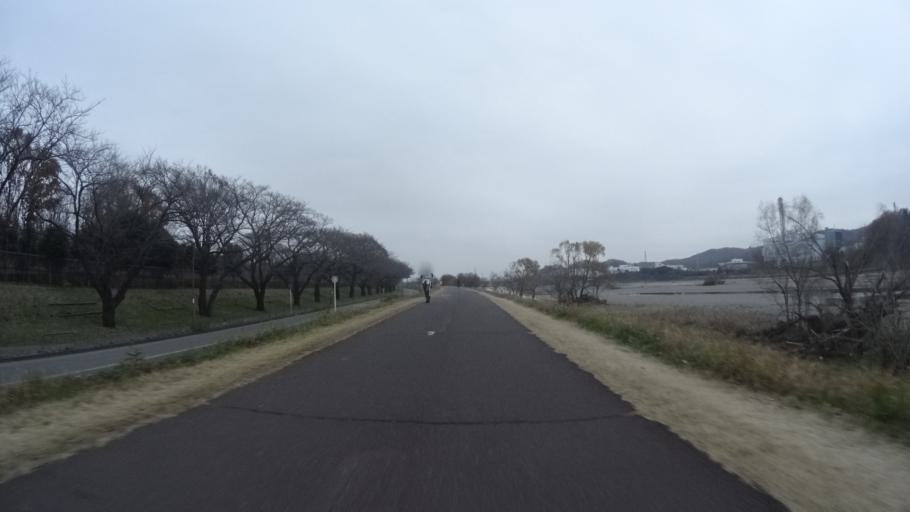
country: JP
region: Tokyo
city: Kokubunji
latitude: 35.6530
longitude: 139.4709
